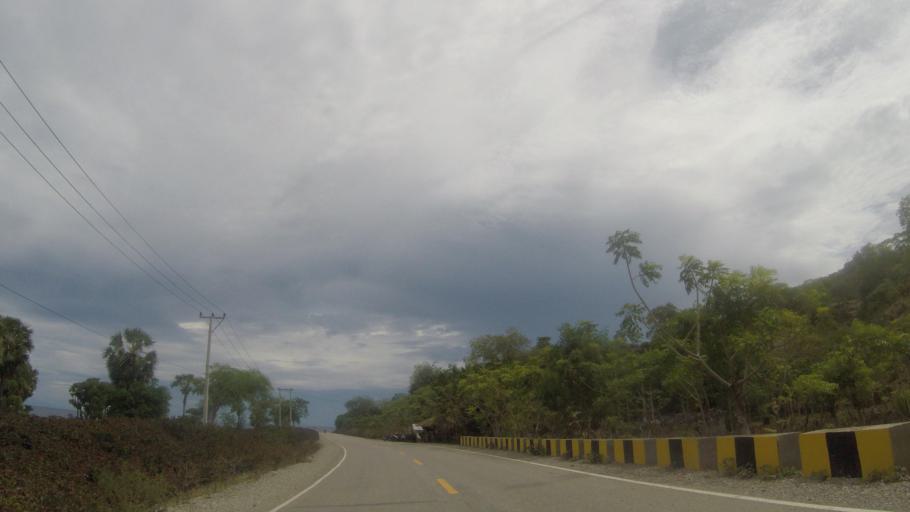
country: TL
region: Baucau
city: Baucau
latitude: -8.4617
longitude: 126.6103
